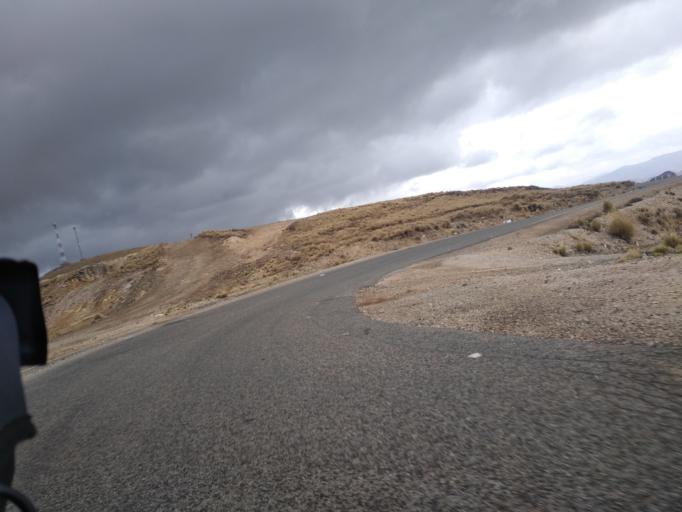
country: PE
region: La Libertad
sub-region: Provincia de Santiago de Chuco
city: Quiruvilca
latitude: -7.9952
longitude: -78.3069
